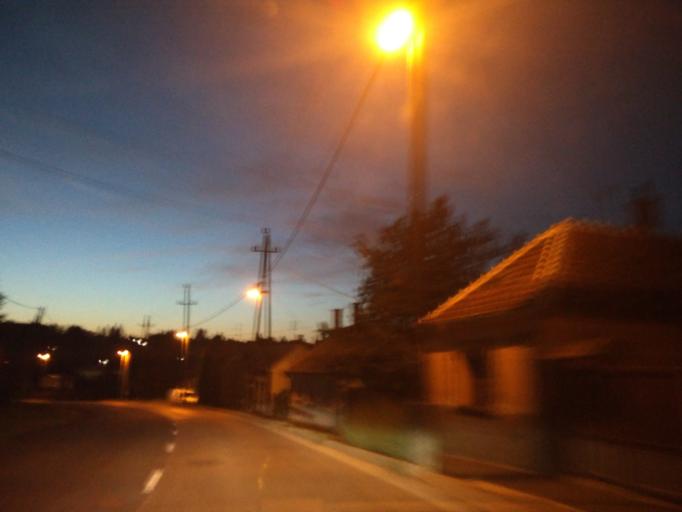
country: HU
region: Vas
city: Vasvar
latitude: 47.0458
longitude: 16.8076
